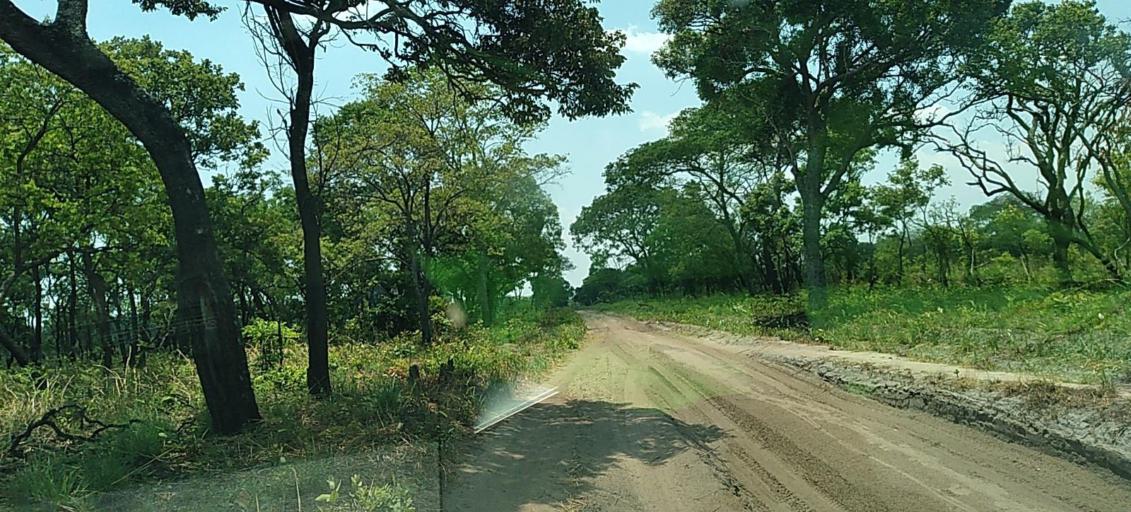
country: CD
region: Katanga
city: Kolwezi
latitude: -11.3111
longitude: 25.2352
